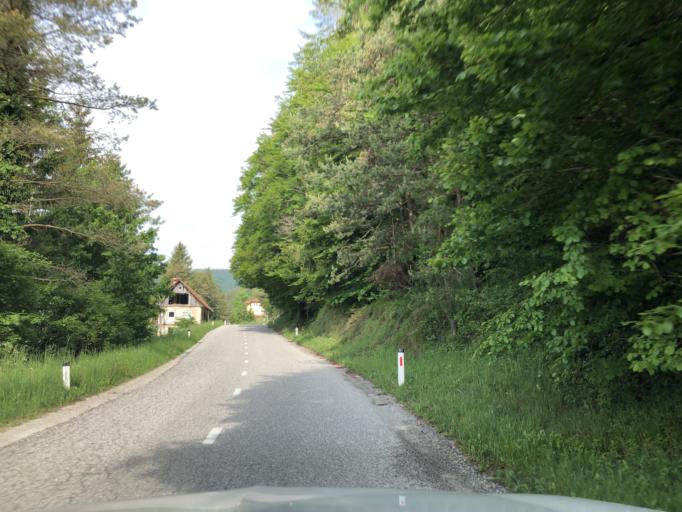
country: SI
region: Velike Lasce
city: Velike Lasce
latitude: 45.8047
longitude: 14.5867
